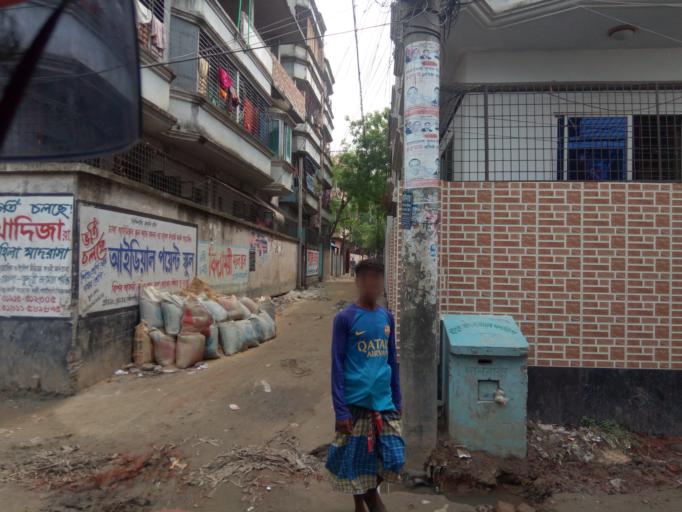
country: BD
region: Dhaka
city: Paltan
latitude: 23.7425
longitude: 90.4489
